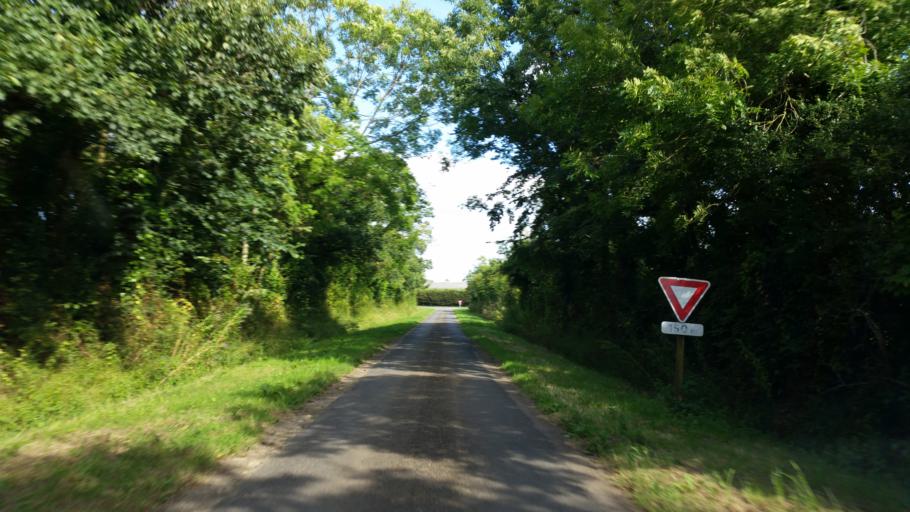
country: FR
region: Lower Normandy
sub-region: Departement de la Manche
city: Sainte-Mere-Eglise
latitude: 49.4508
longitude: -1.2781
